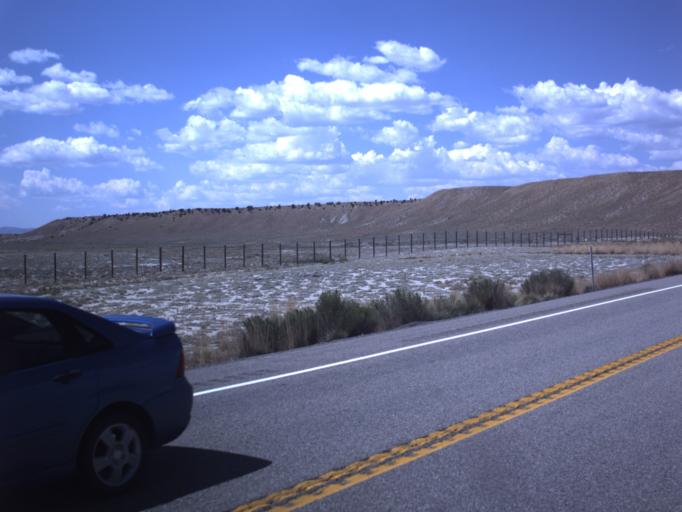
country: US
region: Utah
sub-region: Carbon County
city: Price
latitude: 39.4622
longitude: -110.8593
